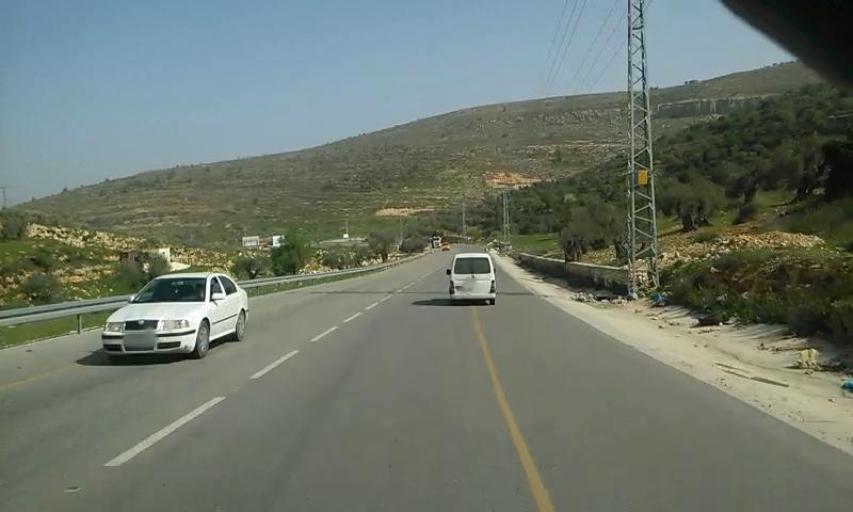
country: PS
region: West Bank
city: Dura al Qar`
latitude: 31.9777
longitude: 35.2346
